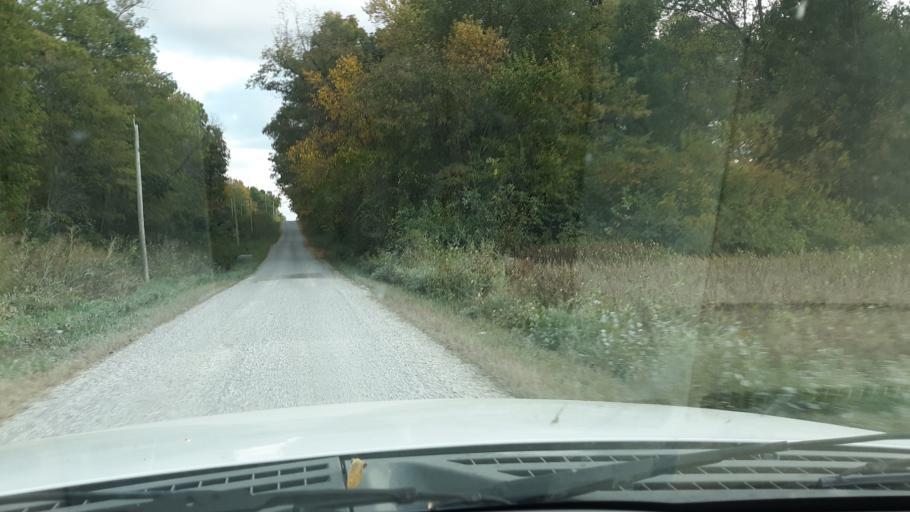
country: US
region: Illinois
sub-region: Saline County
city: Eldorado
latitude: 37.8312
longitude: -88.5026
